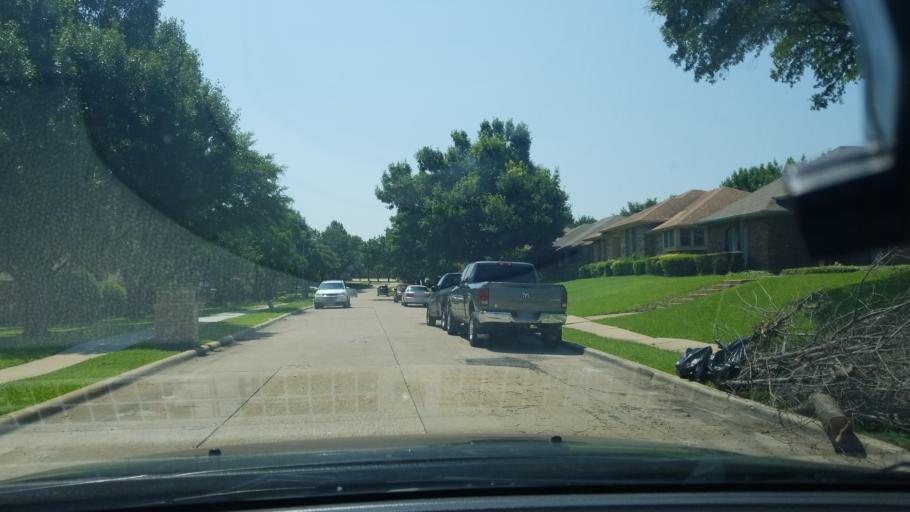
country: US
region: Texas
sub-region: Dallas County
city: Mesquite
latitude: 32.8261
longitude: -96.6175
